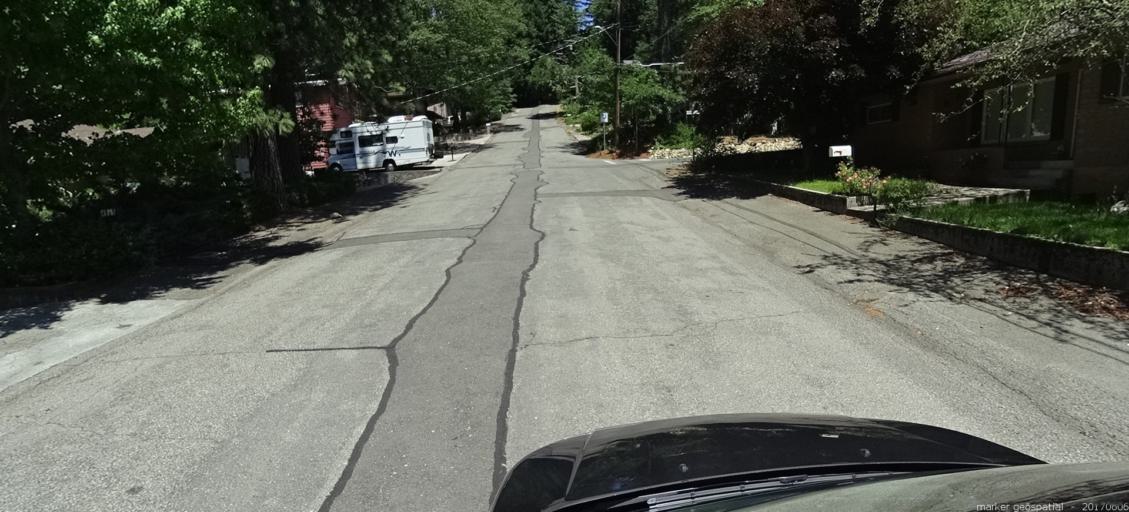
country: US
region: California
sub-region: Siskiyou County
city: Dunsmuir
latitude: 41.2228
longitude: -122.2782
